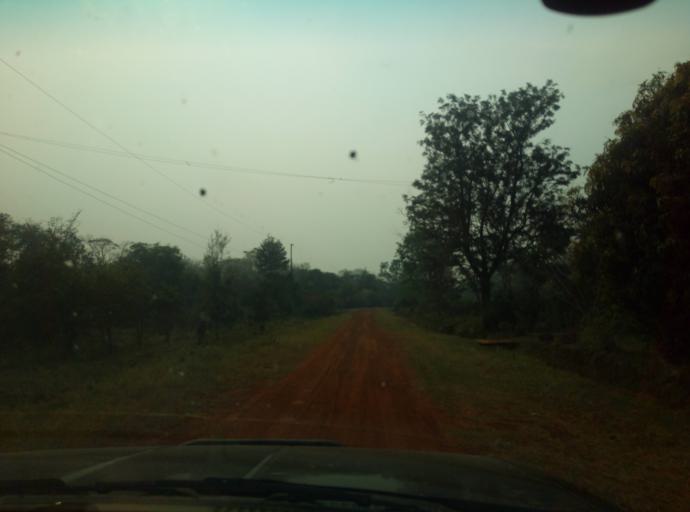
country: PY
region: Caaguazu
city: Carayao
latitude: -25.2038
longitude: -56.2254
